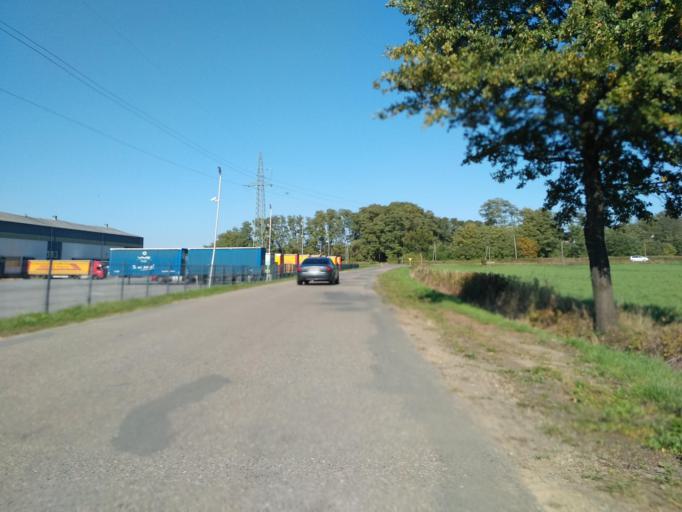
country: PL
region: Subcarpathian Voivodeship
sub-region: Powiat debicki
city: Pilzno
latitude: 49.9853
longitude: 21.3219
